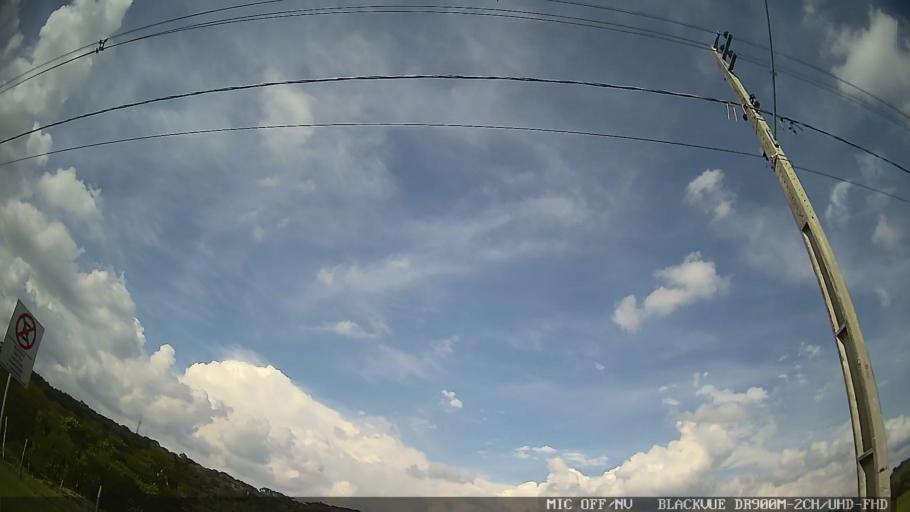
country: BR
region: Sao Paulo
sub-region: Braganca Paulista
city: Braganca Paulista
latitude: -22.9914
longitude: -46.5174
